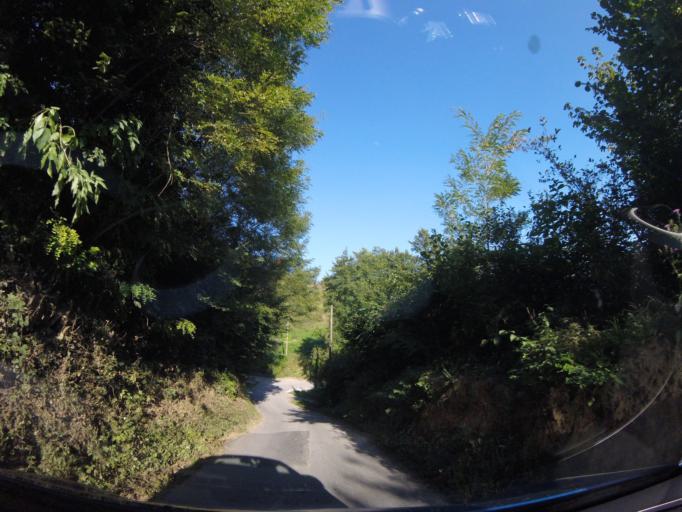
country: HR
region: Zagrebacka
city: Rude
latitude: 45.7639
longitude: 15.6623
